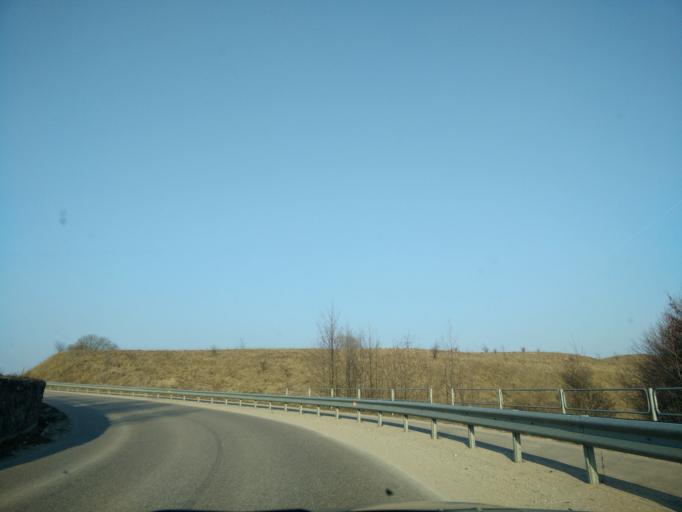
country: LT
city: Trakai
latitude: 54.6727
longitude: 24.9152
